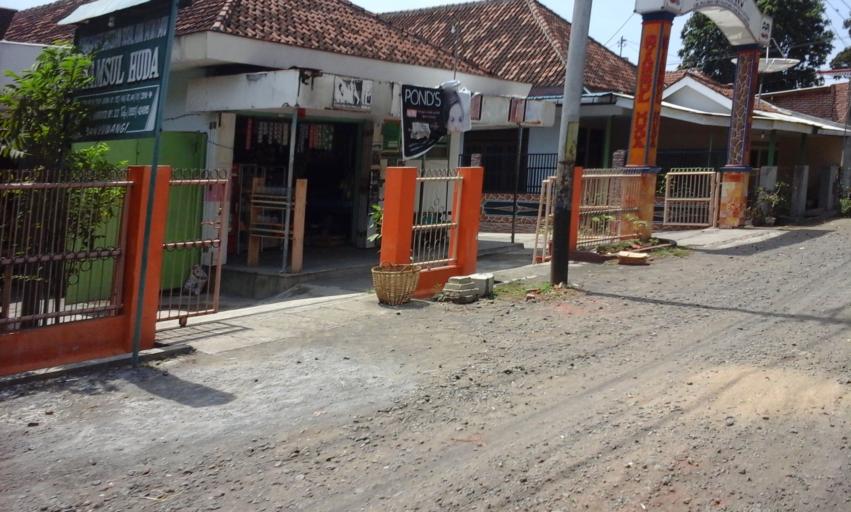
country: ID
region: East Java
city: Klatakan
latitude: -8.1631
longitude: 114.3892
